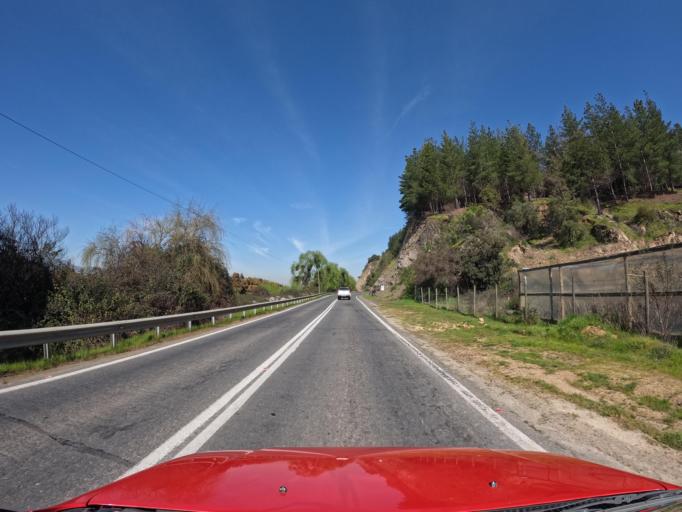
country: CL
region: Maule
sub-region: Provincia de Curico
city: Rauco
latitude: -34.9853
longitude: -71.4247
